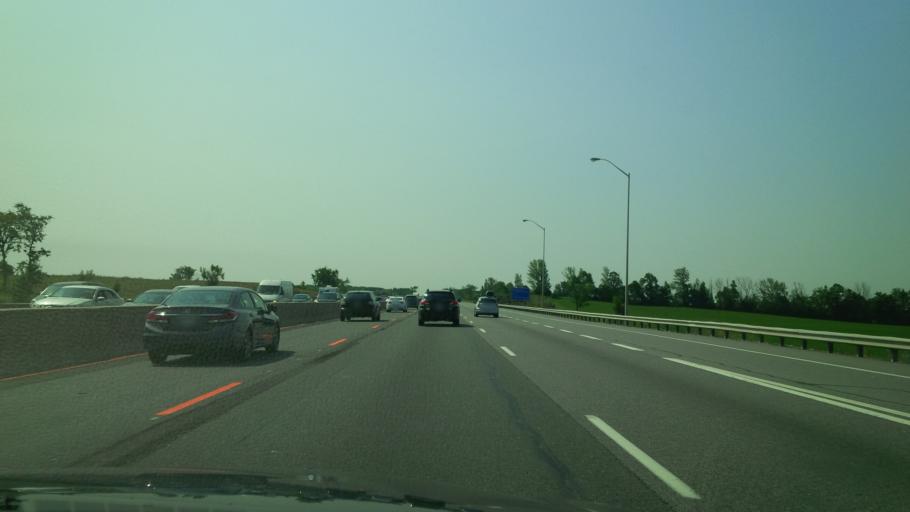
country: CA
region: Ontario
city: Bradford West Gwillimbury
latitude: 44.0237
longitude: -79.5928
